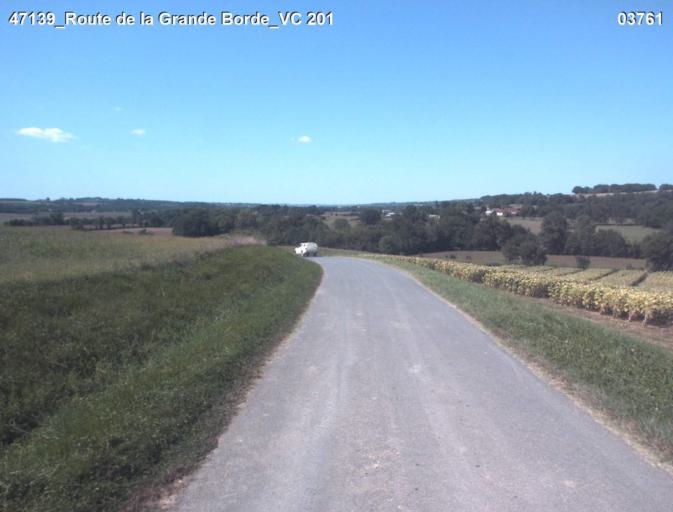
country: FR
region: Aquitaine
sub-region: Departement du Lot-et-Garonne
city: Nerac
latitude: 44.0919
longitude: 0.3776
